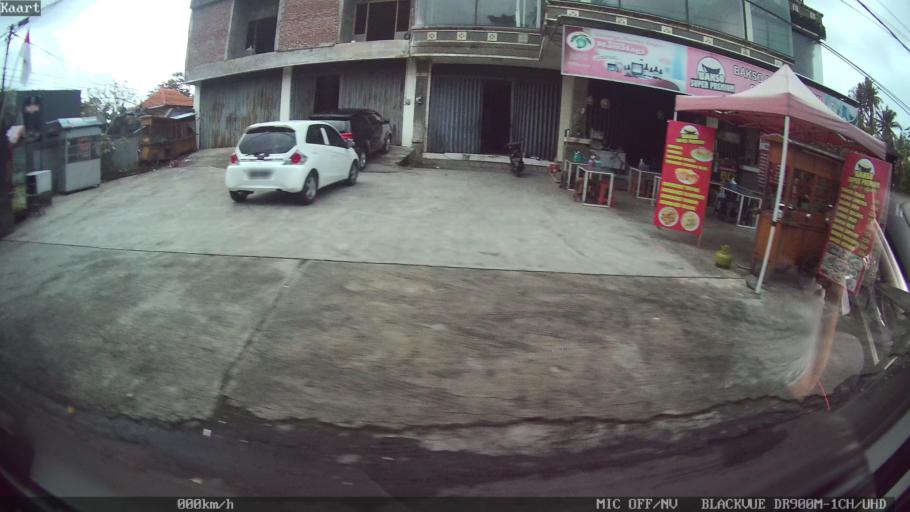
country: ID
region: Bali
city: Banjar Mambalkajanan
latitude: -8.5592
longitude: 115.2187
